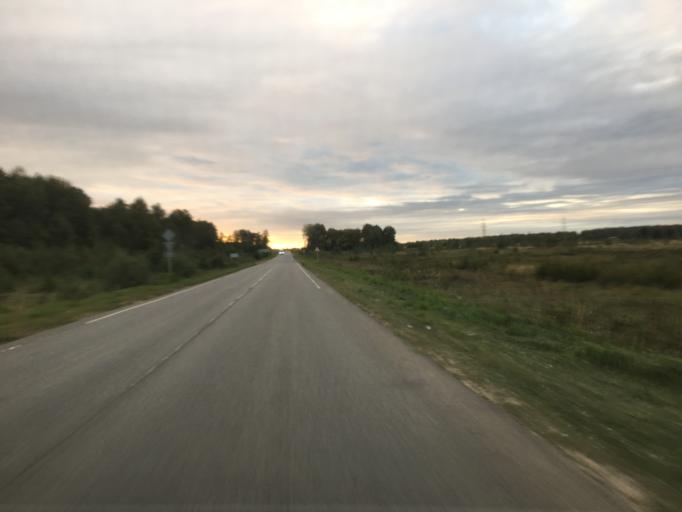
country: RU
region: Kaluga
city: Kaluga
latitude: 54.5858
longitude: 36.3701
